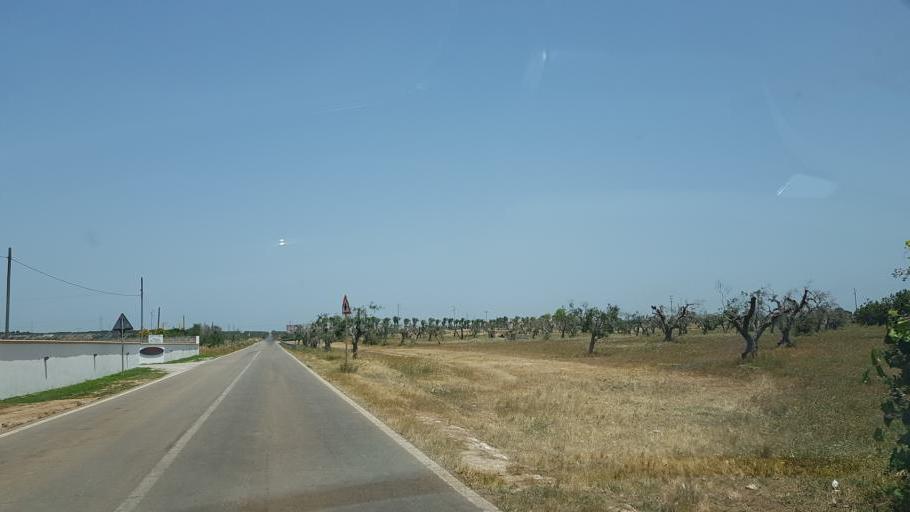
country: IT
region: Apulia
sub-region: Provincia di Lecce
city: Porto Cesareo
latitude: 40.2786
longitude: 17.9049
